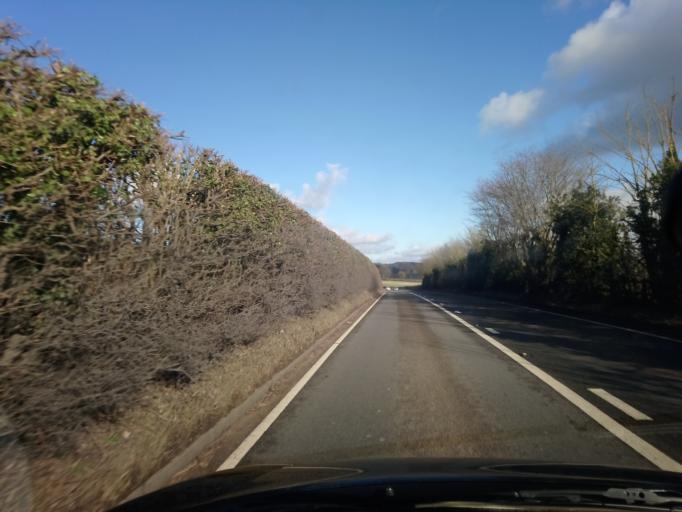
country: GB
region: England
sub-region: Shropshire
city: Clive
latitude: 52.8120
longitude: -2.6895
